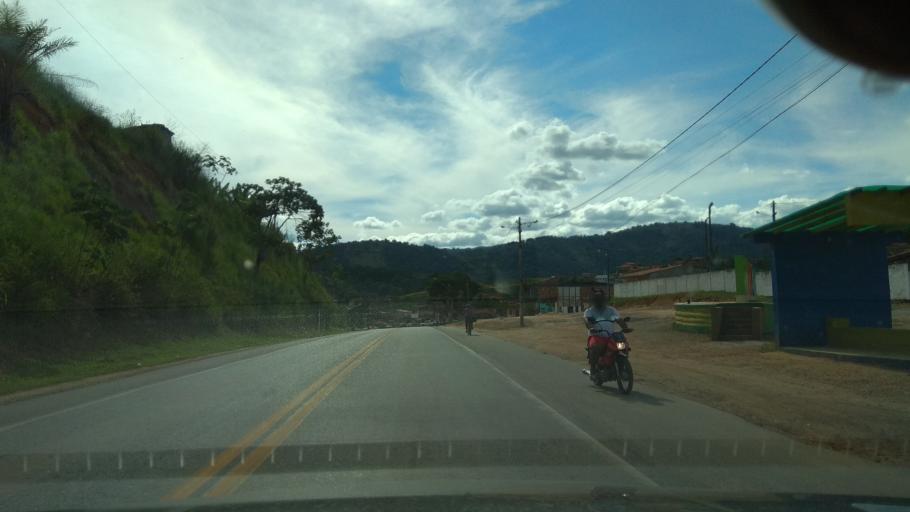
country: BR
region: Bahia
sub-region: Jitauna
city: Jitauna
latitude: -14.0108
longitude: -39.8950
